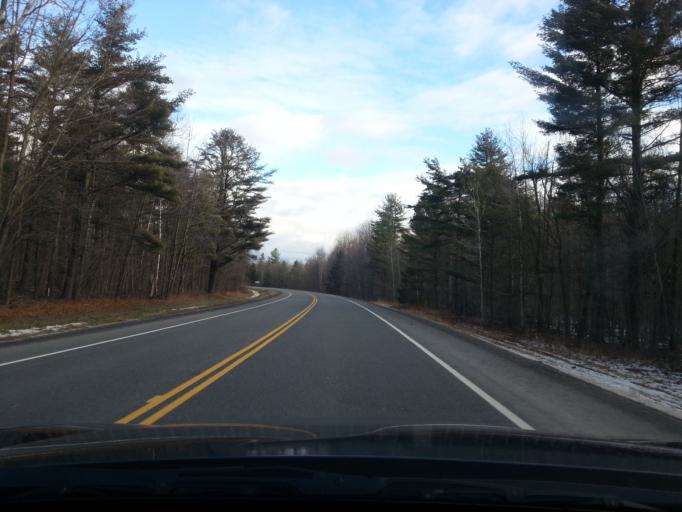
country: CA
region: Ontario
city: Prescott
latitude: 45.0473
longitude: -75.5594
